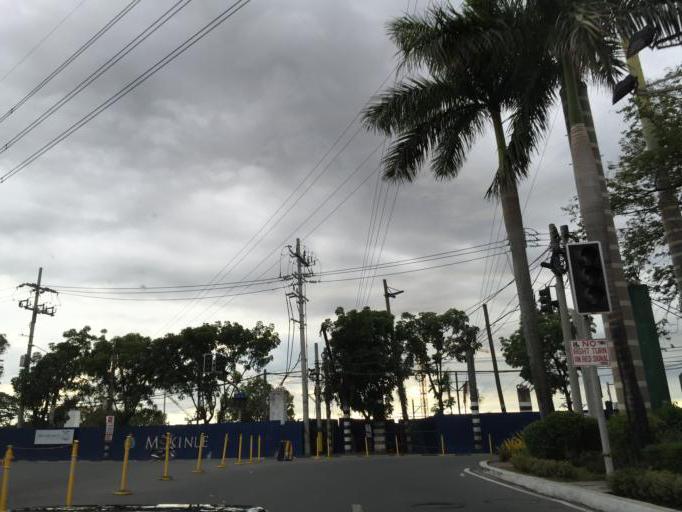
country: PH
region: Metro Manila
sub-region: Makati City
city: Makati City
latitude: 14.5357
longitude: 121.0468
